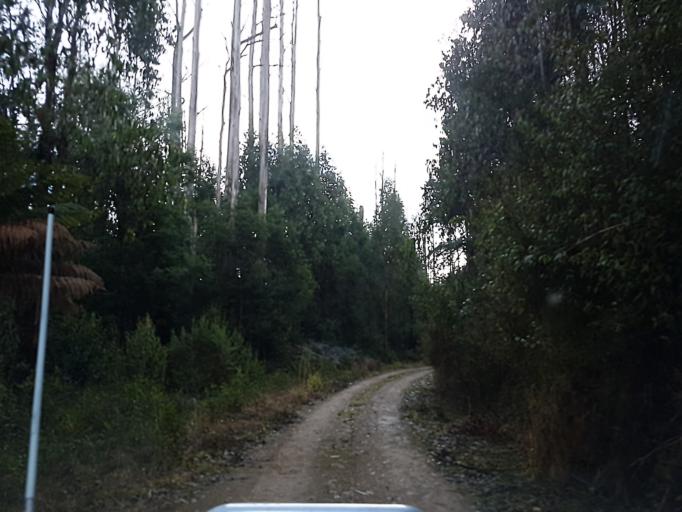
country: AU
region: Victoria
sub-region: Yarra Ranges
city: Millgrove
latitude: -37.5485
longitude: 145.7464
